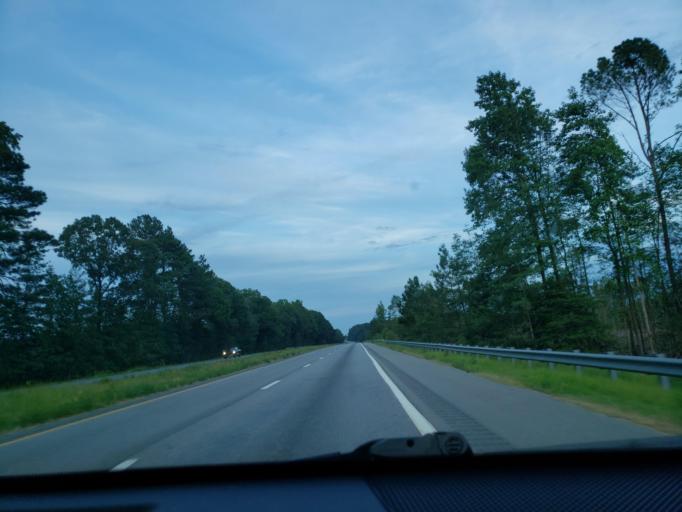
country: US
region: Virginia
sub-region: Sussex County
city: Sussex
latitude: 36.7049
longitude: -77.2835
